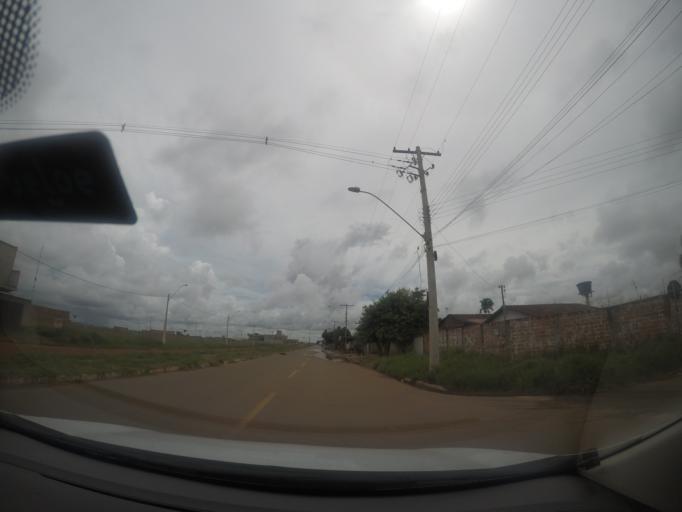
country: BR
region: Goias
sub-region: Trindade
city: Trindade
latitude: -16.6984
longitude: -49.4104
